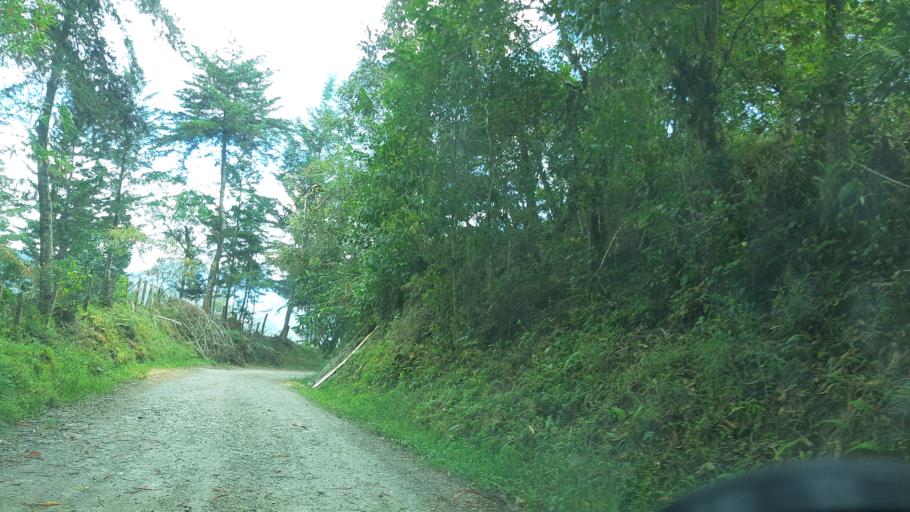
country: CO
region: Boyaca
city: Garagoa
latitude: 5.0488
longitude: -73.3541
